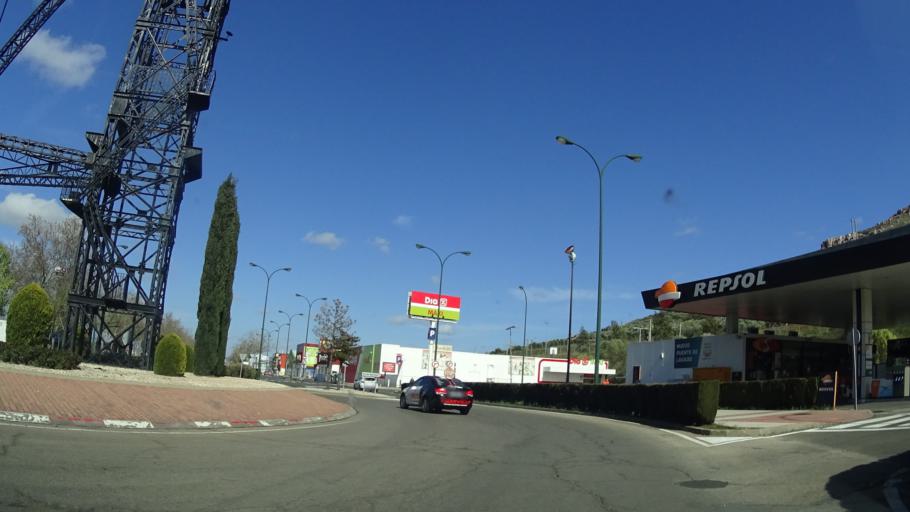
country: ES
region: Castille-La Mancha
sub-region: Provincia de Ciudad Real
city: Puertollano
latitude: 38.6977
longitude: -4.1062
